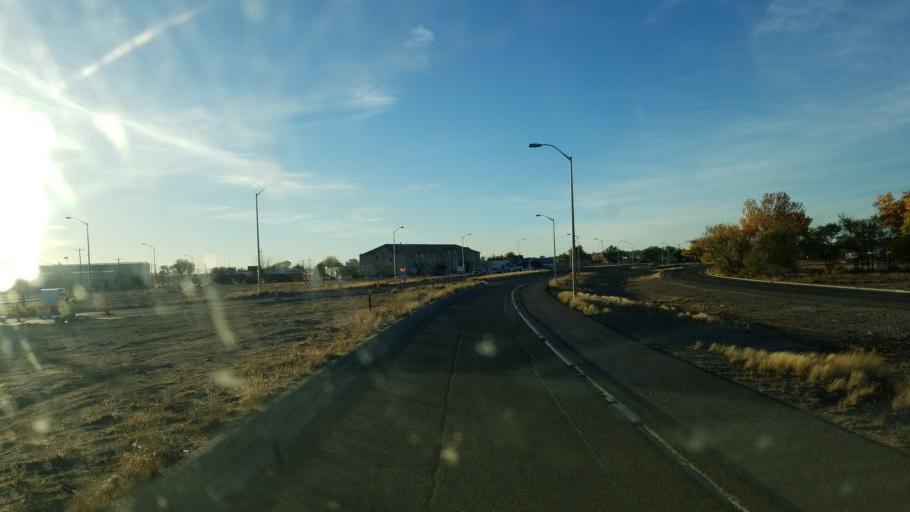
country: US
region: New Mexico
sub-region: San Juan County
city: Farmington
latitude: 36.7197
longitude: -108.1823
